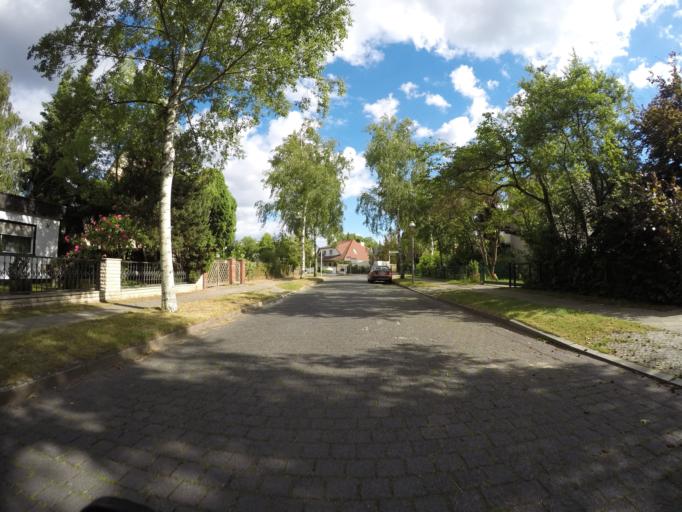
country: DE
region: Berlin
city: Zehlendorf Bezirk
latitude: 52.4256
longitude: 13.2680
